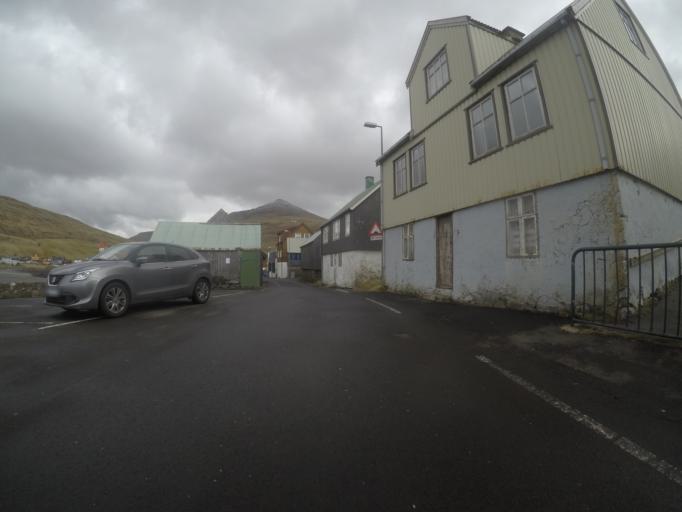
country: FO
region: Vagar
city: Midvagur
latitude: 62.0517
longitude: -7.1510
